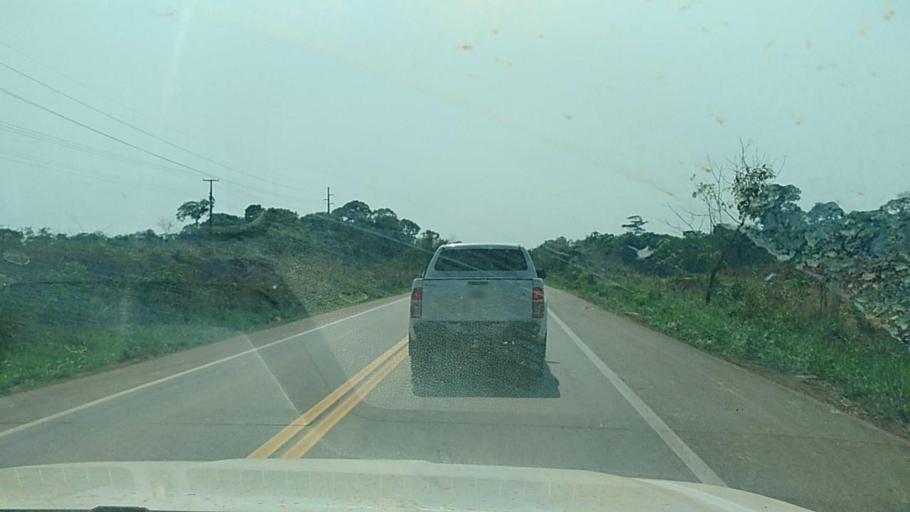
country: BR
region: Rondonia
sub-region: Porto Velho
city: Porto Velho
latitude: -8.7894
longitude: -63.6225
